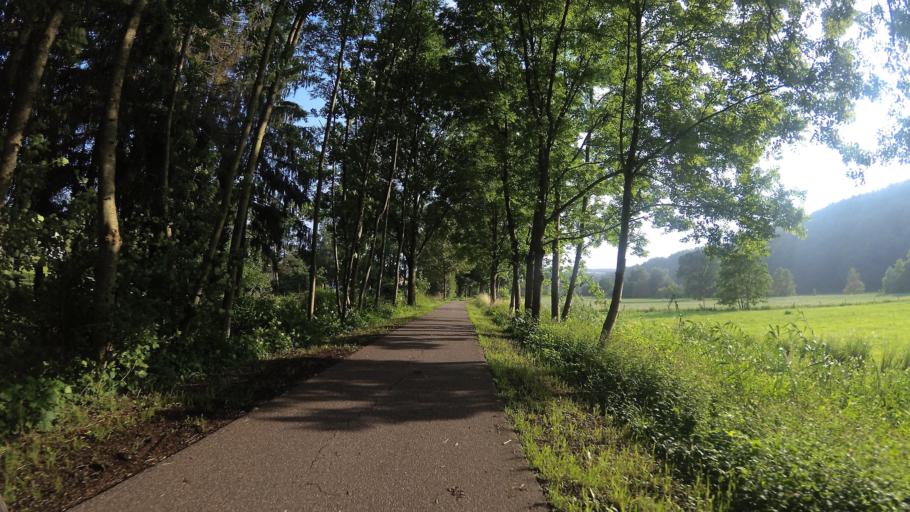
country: DE
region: Rheinland-Pfalz
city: Althornbach
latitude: 49.2182
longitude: 7.3719
